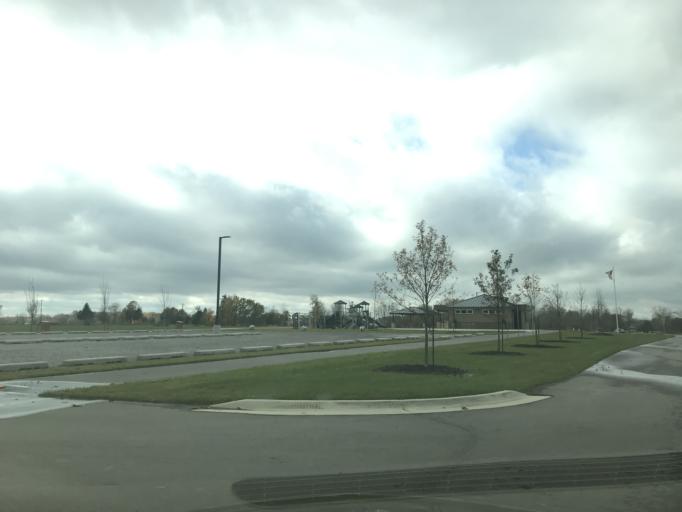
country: US
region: Michigan
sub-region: Eaton County
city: Grand Ledge
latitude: 42.7141
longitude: -84.6947
